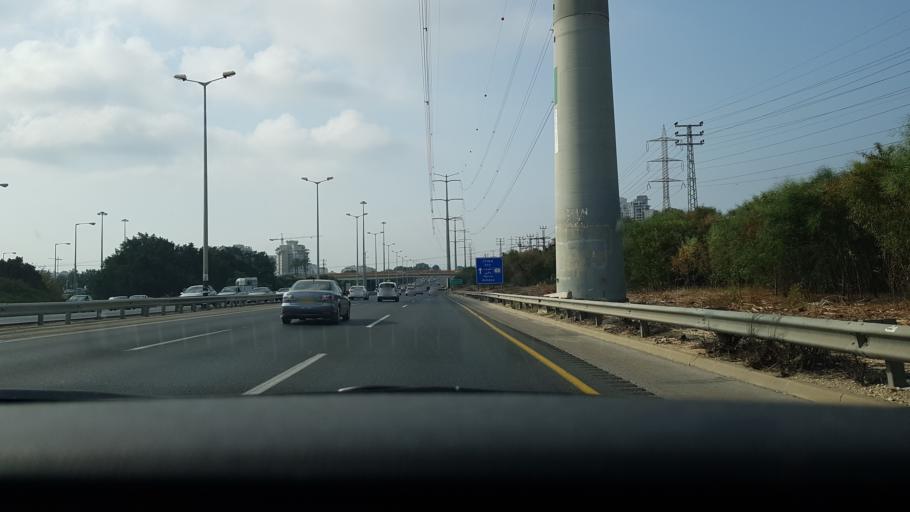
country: IL
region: Central District
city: Rishon LeZiyyon
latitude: 31.9802
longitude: 34.7936
